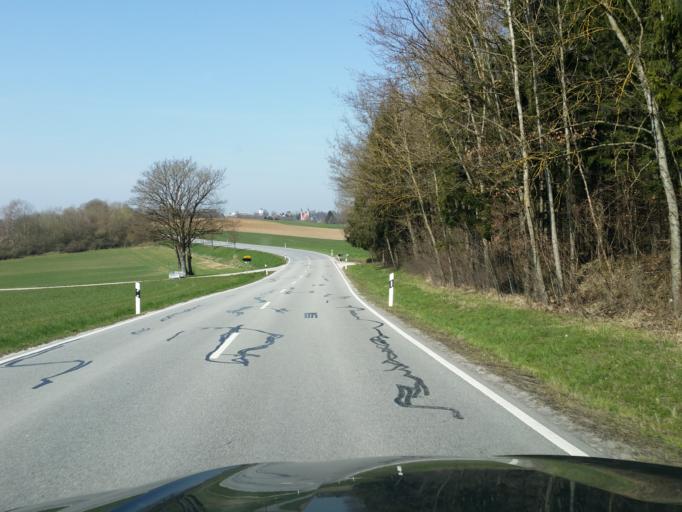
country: DE
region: Bavaria
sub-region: Lower Bavaria
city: Landshut
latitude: 48.5262
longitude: 12.1865
